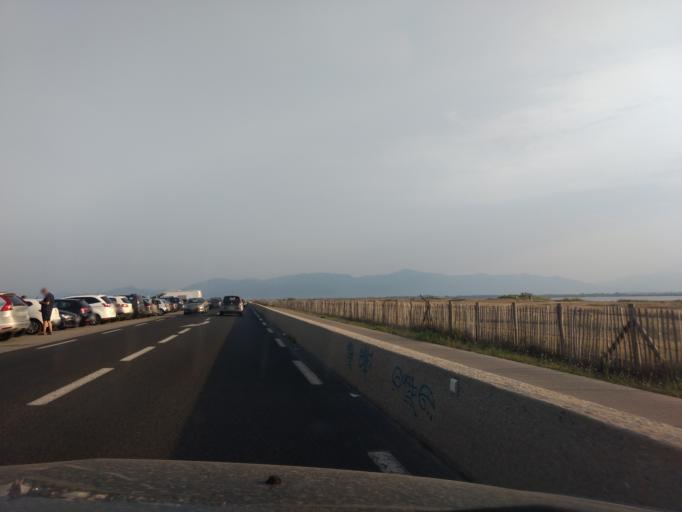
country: FR
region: Languedoc-Roussillon
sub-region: Departement des Pyrenees-Orientales
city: Canet-en-Roussillon
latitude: 42.6707
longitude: 3.0332
